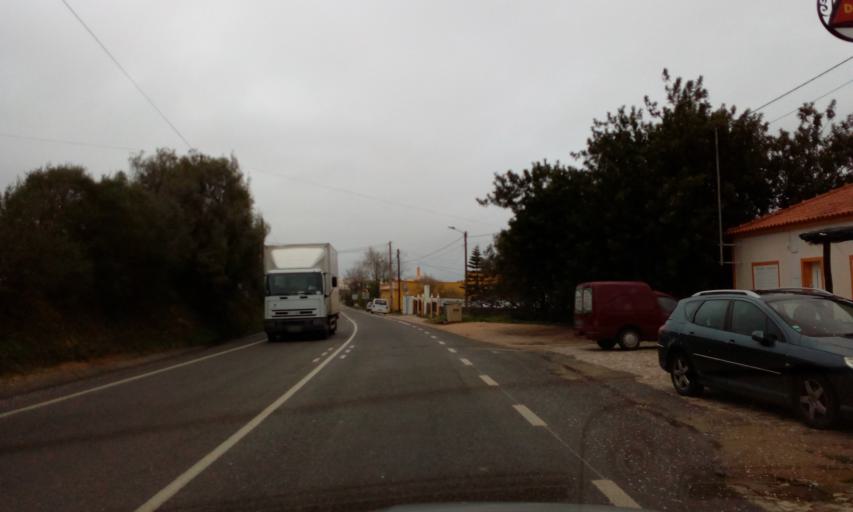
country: PT
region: Faro
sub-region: Albufeira
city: Guia
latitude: 37.1551
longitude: -8.2819
